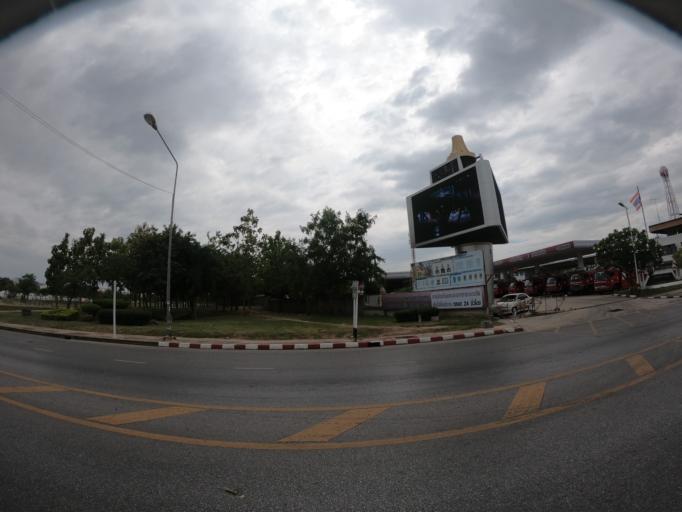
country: TH
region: Roi Et
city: Roi Et
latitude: 16.0542
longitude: 103.6429
